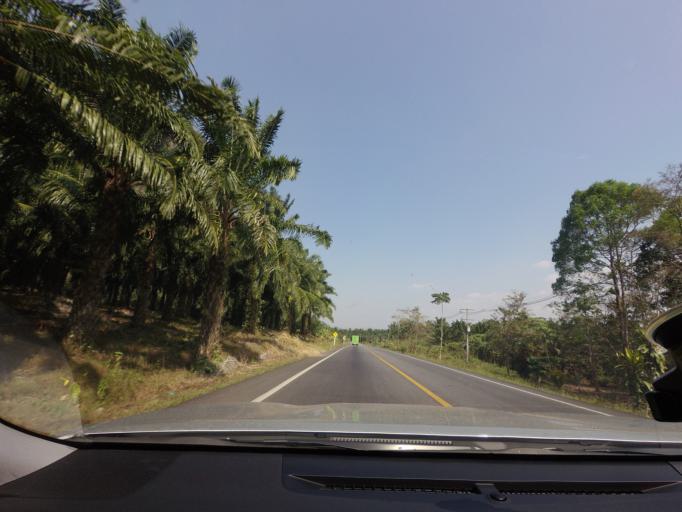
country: TH
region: Krabi
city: Plai Phraya
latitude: 8.5558
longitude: 98.7891
